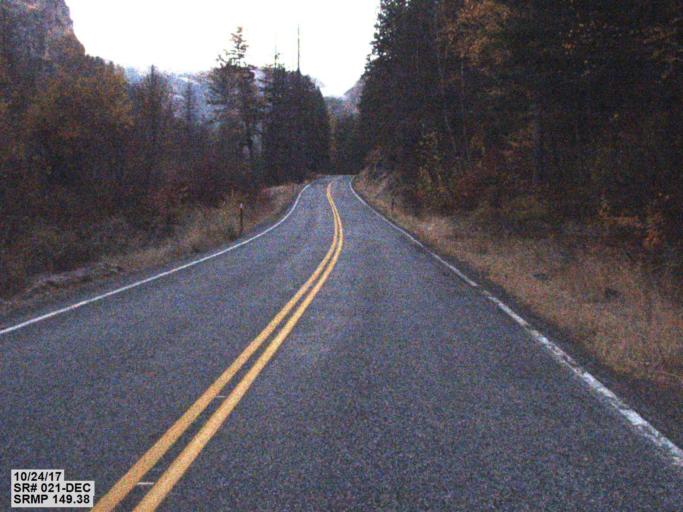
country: US
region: Washington
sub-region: Ferry County
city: Republic
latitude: 48.4964
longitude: -118.7411
